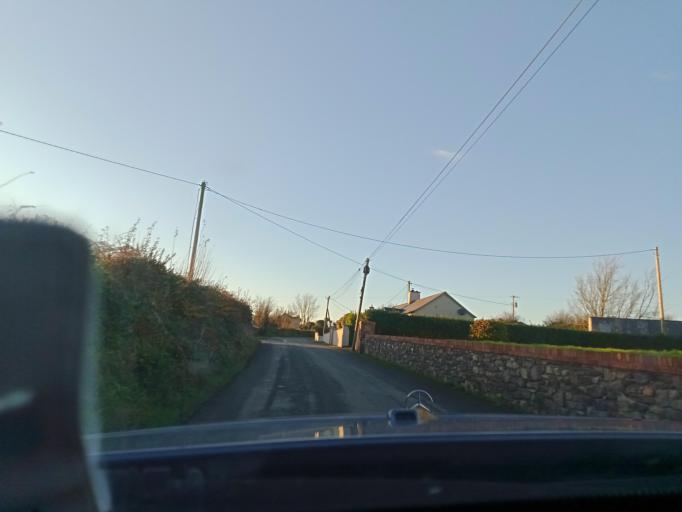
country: IE
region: Leinster
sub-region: Loch Garman
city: New Ross
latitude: 52.3702
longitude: -7.0341
